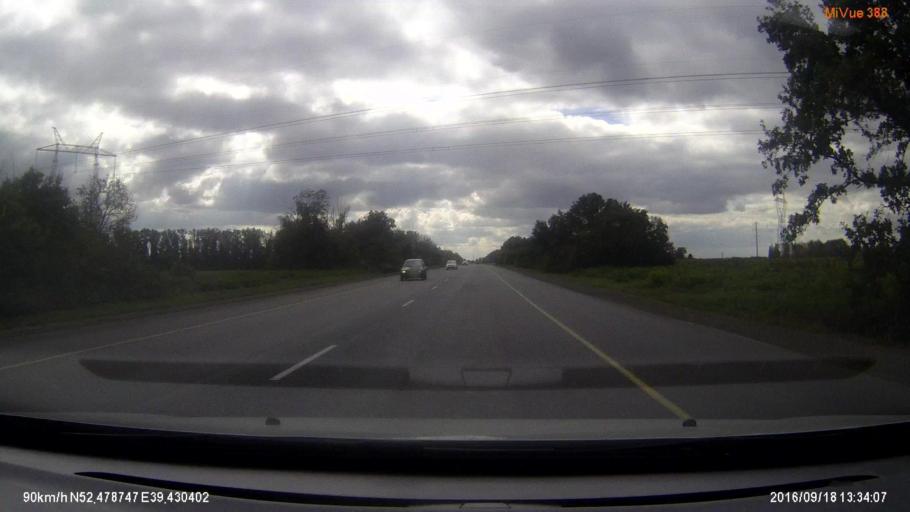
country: RU
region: Lipetsk
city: Borinskoye
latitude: 52.4846
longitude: 39.4379
